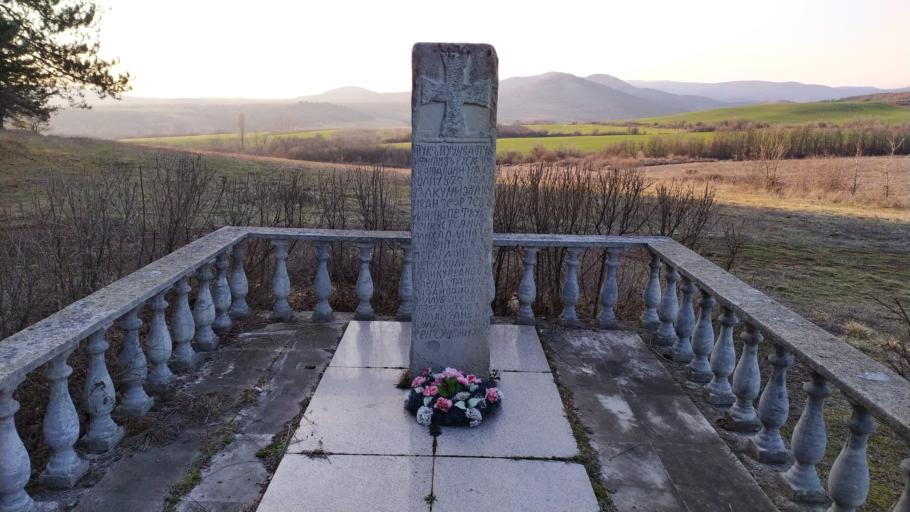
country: BG
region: Stara Zagora
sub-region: Obshtina Nikolaevo
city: Elkhovo
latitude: 42.4064
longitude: 25.3832
